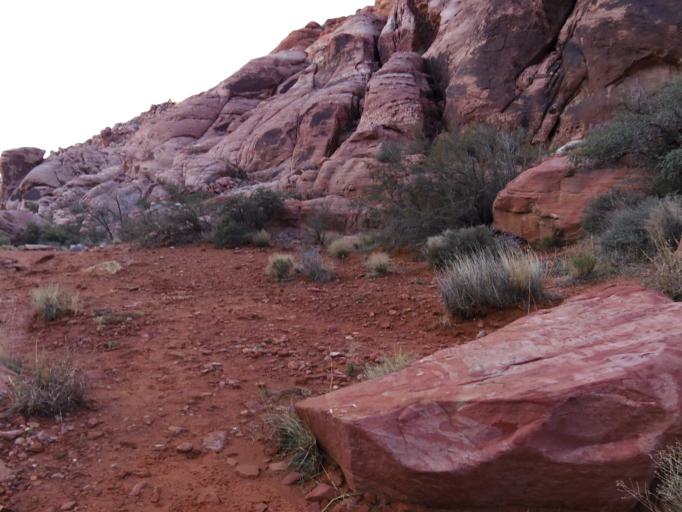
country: US
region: Nevada
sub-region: Clark County
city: Summerlin South
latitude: 36.1517
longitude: -115.4280
